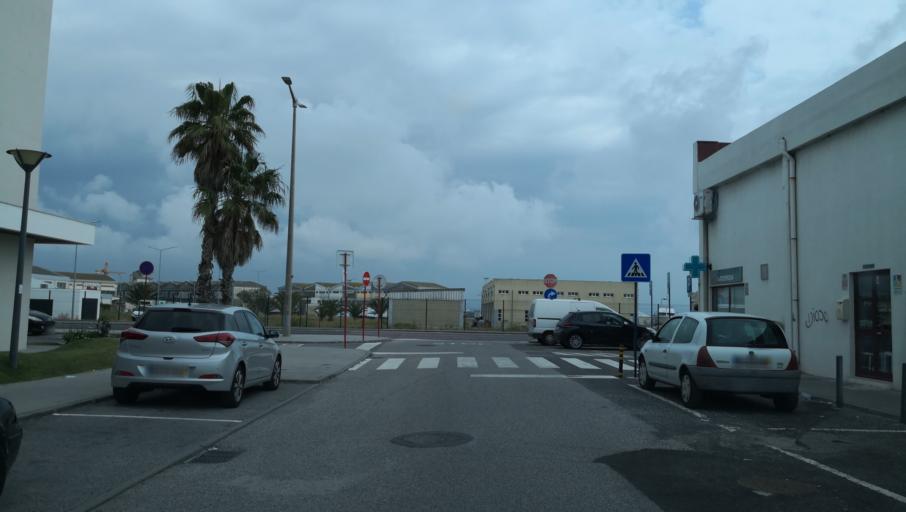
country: PT
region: Leiria
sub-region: Peniche
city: Peniche
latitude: 39.3580
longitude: -9.3750
